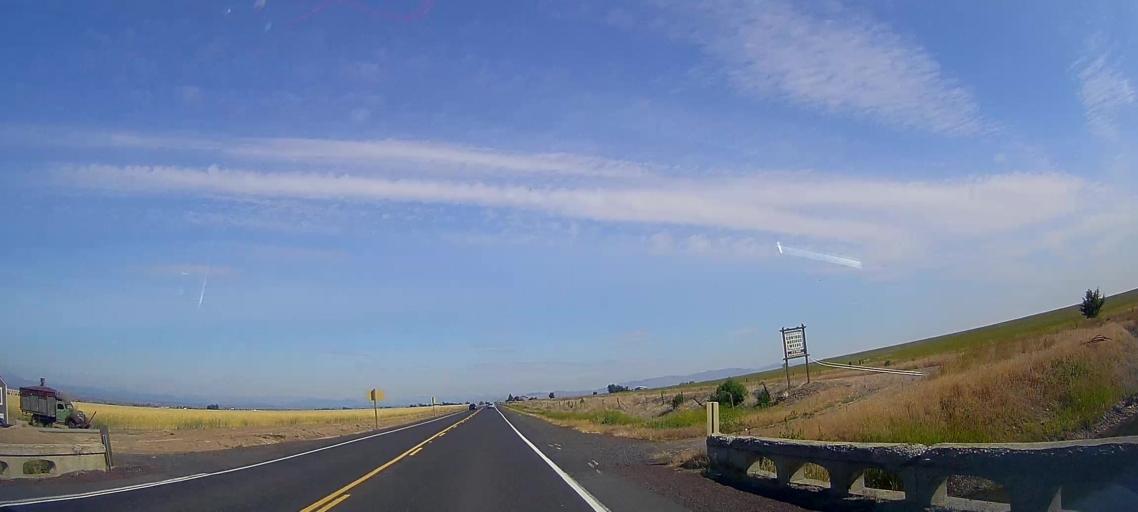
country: US
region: Oregon
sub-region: Jefferson County
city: Madras
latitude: 44.6683
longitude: -121.1385
